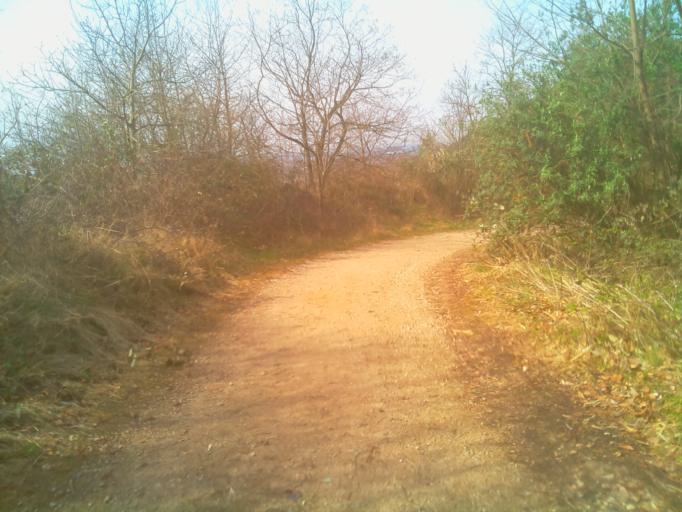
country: DE
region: Baden-Wuerttemberg
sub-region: Karlsruhe Region
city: Dossenheim
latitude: 49.4459
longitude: 8.6844
